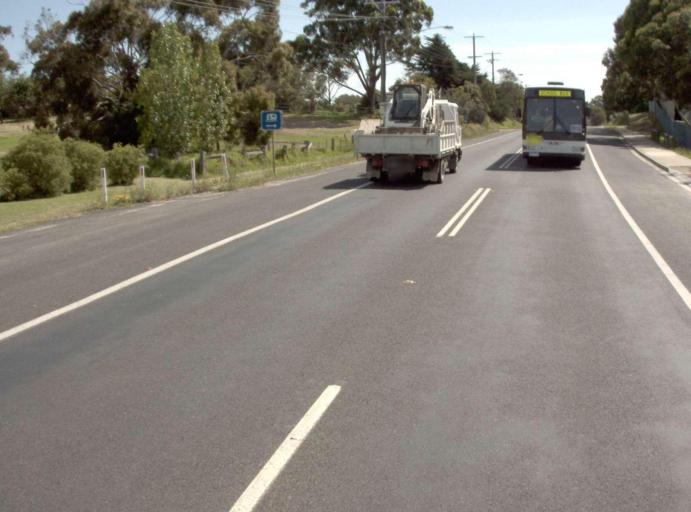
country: AU
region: Victoria
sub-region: East Gippsland
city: Bairnsdale
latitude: -37.8167
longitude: 147.7383
